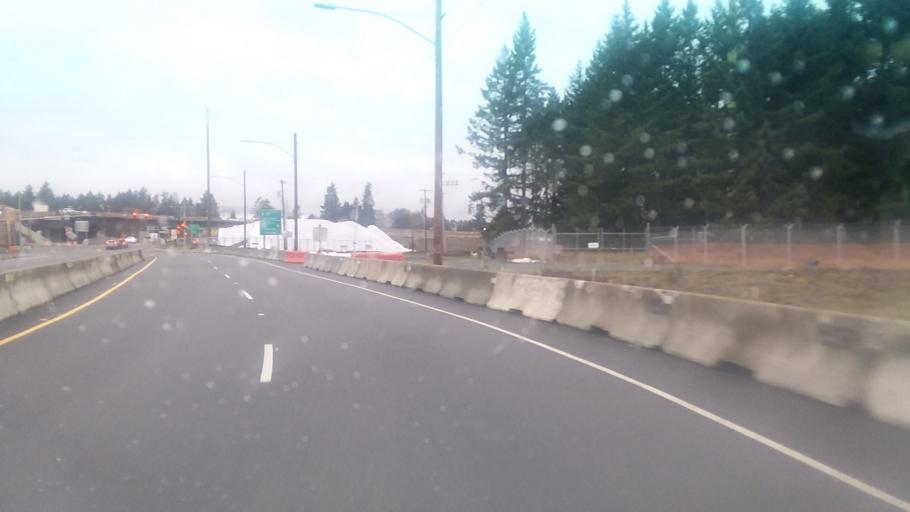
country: US
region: Washington
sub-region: Pierce County
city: Fort Lewis
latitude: 47.1171
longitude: -122.5547
